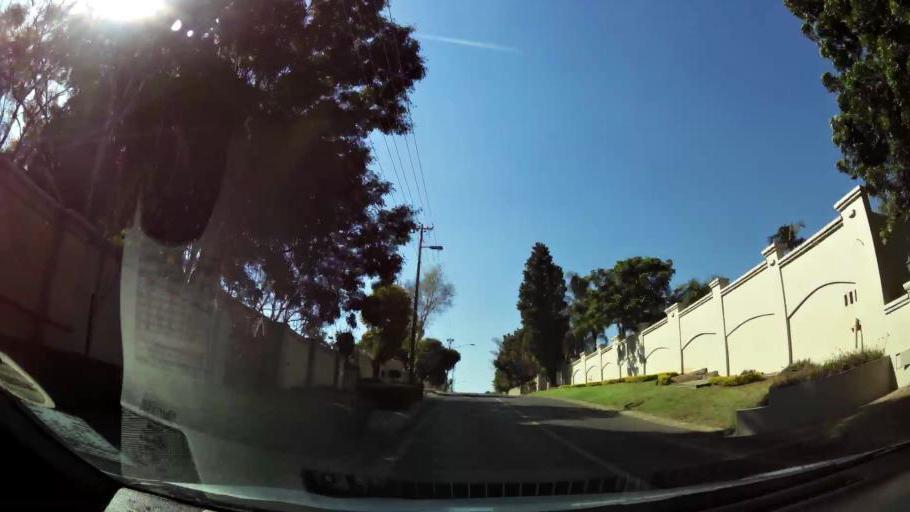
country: ZA
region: Gauteng
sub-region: City of Tshwane Metropolitan Municipality
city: Pretoria
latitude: -25.7965
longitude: 28.2387
